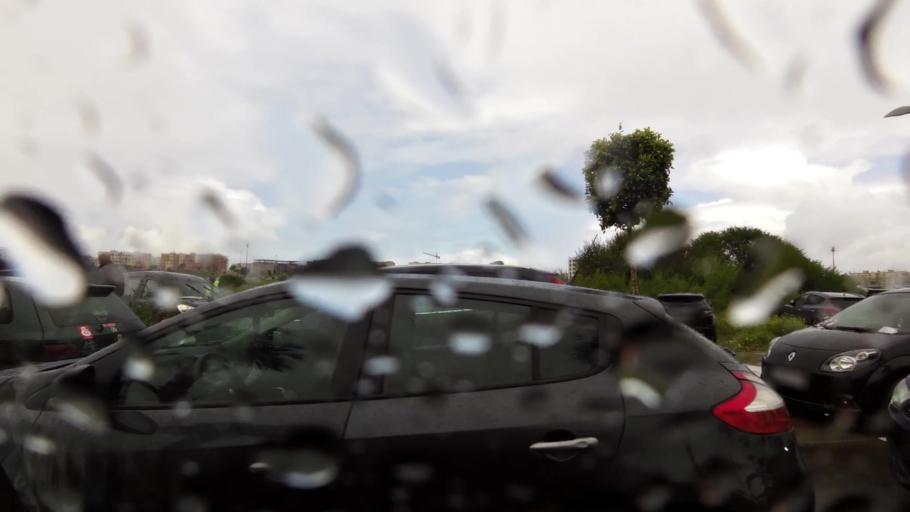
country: MA
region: Grand Casablanca
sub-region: Casablanca
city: Casablanca
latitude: 33.5484
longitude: -7.6677
